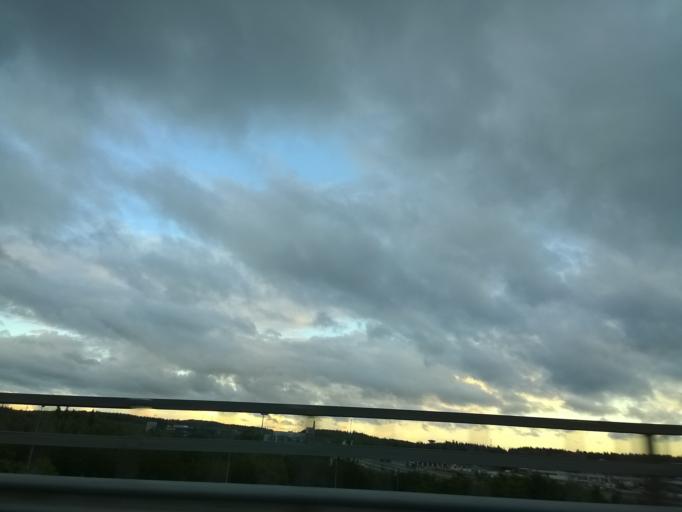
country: FI
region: Pirkanmaa
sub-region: Tampere
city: Tampere
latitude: 61.4619
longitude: 23.7731
